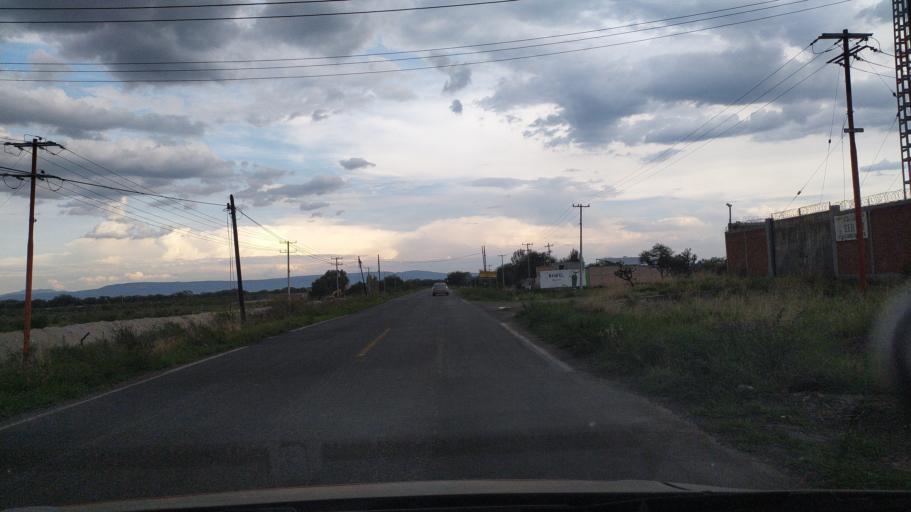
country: MX
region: Guanajuato
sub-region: San Francisco del Rincon
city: San Ignacio de Hidalgo
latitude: 20.8253
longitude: -101.9032
